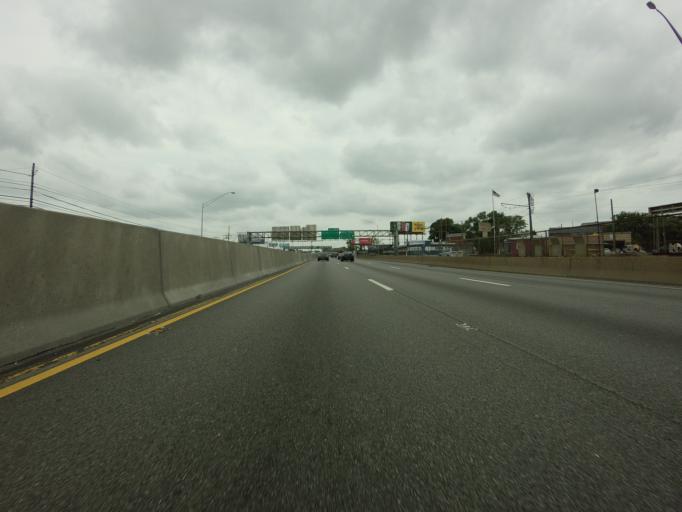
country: US
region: Pennsylvania
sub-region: Philadelphia County
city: Philadelphia
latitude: 39.9271
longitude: -75.1950
